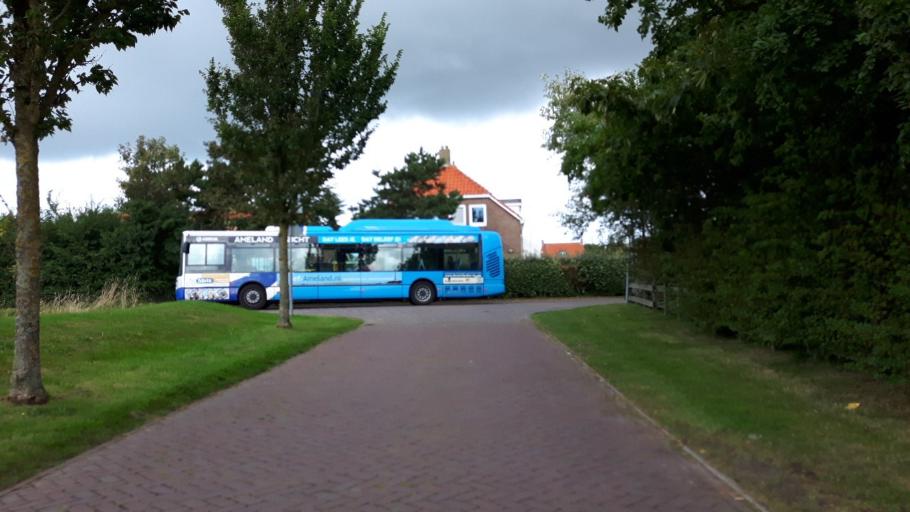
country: NL
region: Friesland
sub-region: Gemeente Ameland
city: Hollum
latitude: 53.4423
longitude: 5.6356
